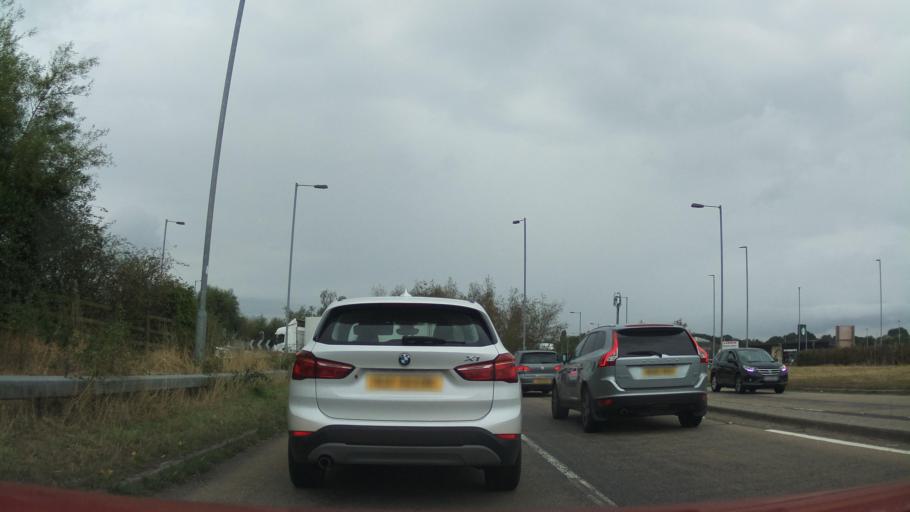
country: GB
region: England
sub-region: Nottinghamshire
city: South Collingham
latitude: 53.0944
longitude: -0.7785
